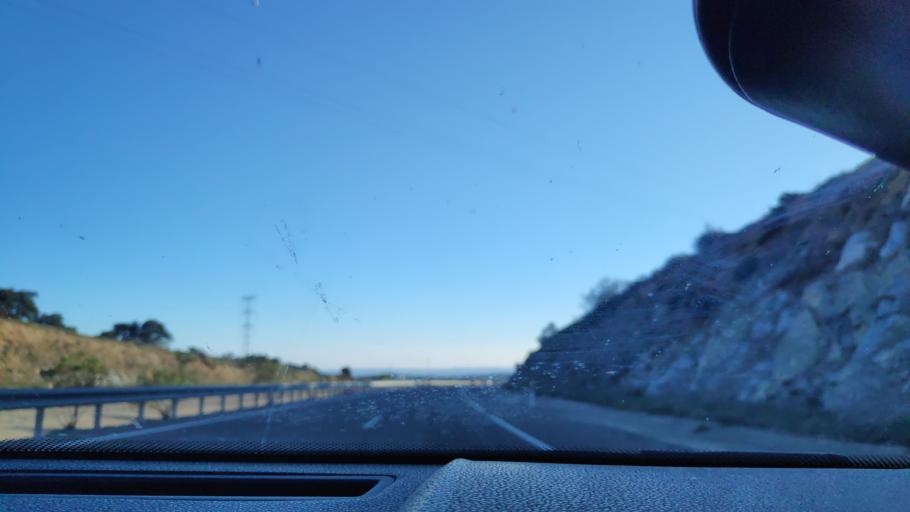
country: ES
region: Andalusia
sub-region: Provincia de Sevilla
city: Gerena
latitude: 37.5976
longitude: -6.1240
